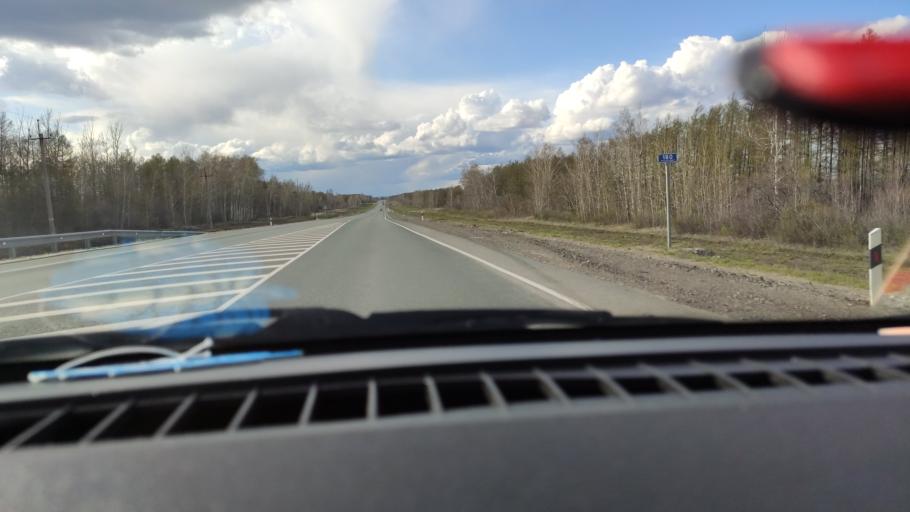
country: RU
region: Saratov
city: Shikhany
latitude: 52.1537
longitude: 47.1829
